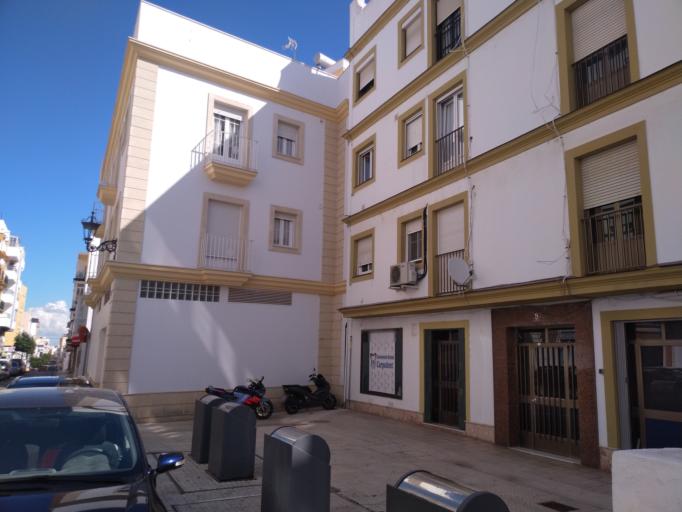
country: ES
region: Andalusia
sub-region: Provincia de Cadiz
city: San Fernando
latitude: 36.4697
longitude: -6.1976
